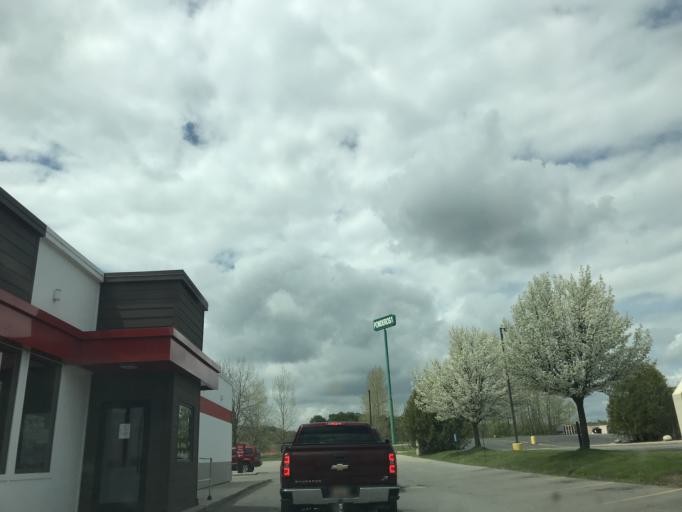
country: US
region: Michigan
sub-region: Ogemaw County
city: West Branch
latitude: 44.2521
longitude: -84.2260
